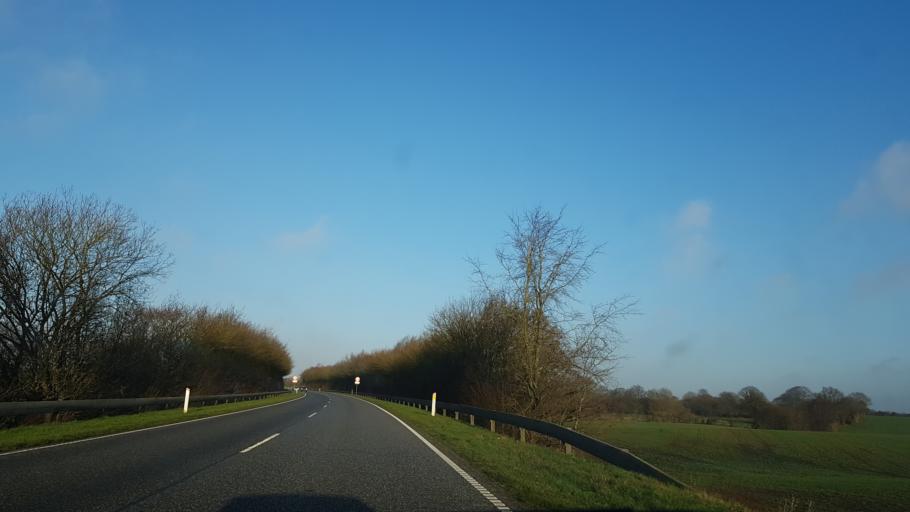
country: DK
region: South Denmark
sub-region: Haderslev Kommune
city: Haderslev
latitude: 55.2067
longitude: 9.4578
